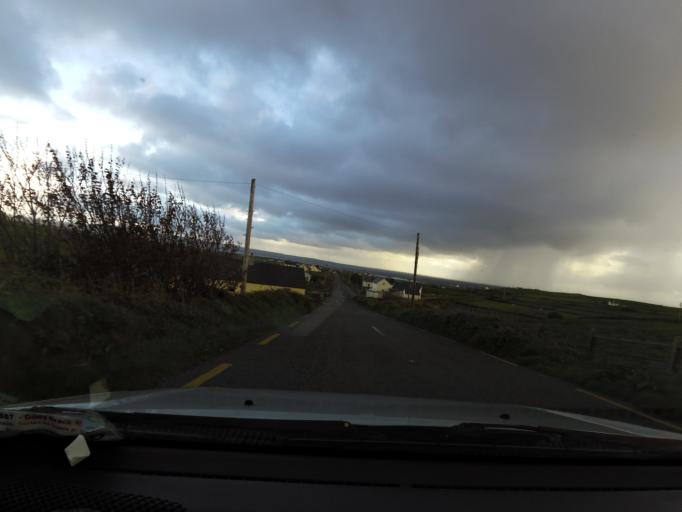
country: IE
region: Munster
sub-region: An Clar
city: Kilrush
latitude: 52.9474
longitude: -9.4252
